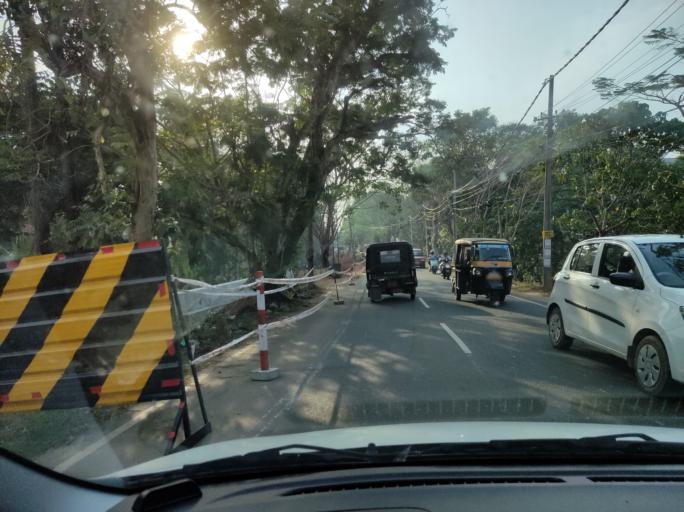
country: IN
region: Kerala
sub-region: Kottayam
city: Kottayam
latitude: 9.6305
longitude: 76.5282
